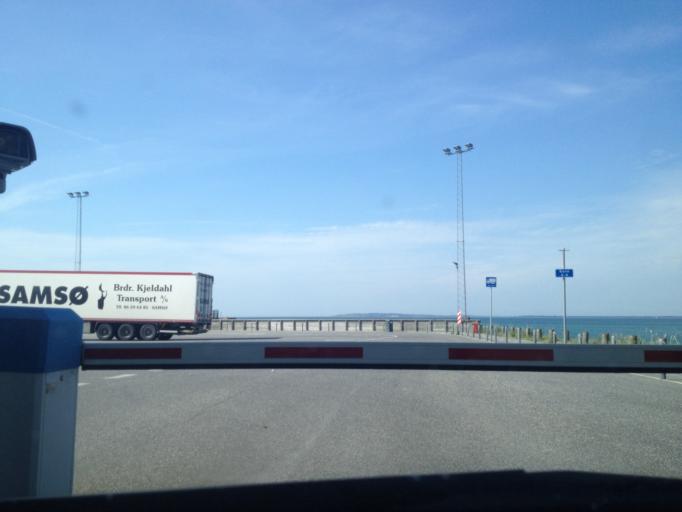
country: DK
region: Central Jutland
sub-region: Samso Kommune
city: Tranebjerg
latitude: 55.8636
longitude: 10.5499
